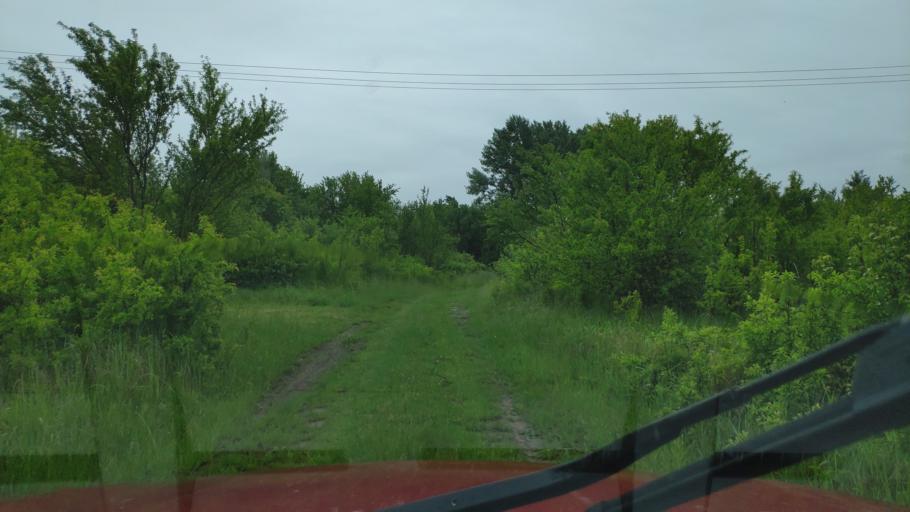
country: SK
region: Kosicky
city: Cierna nad Tisou
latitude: 48.4153
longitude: 22.0221
